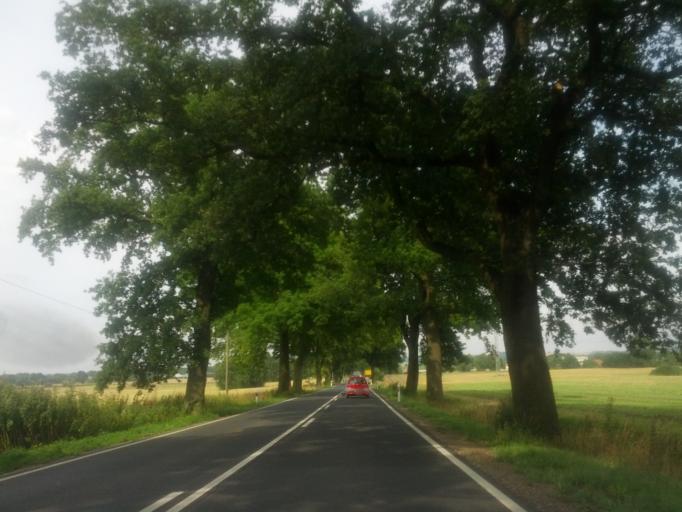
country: DE
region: Mecklenburg-Vorpommern
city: Hornstorf
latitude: 53.9082
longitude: 11.5720
